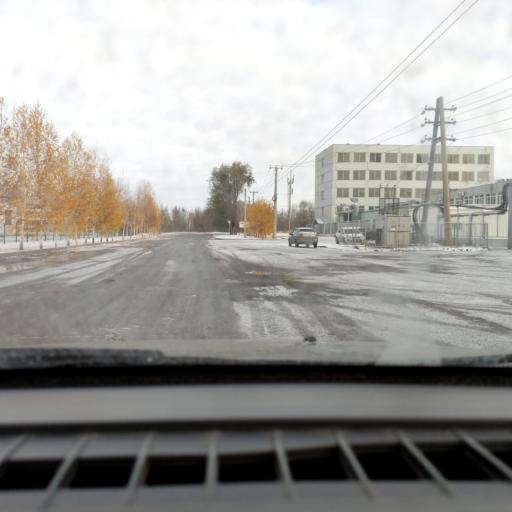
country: RU
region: Samara
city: Tol'yatti
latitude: 53.5779
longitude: 49.2844
